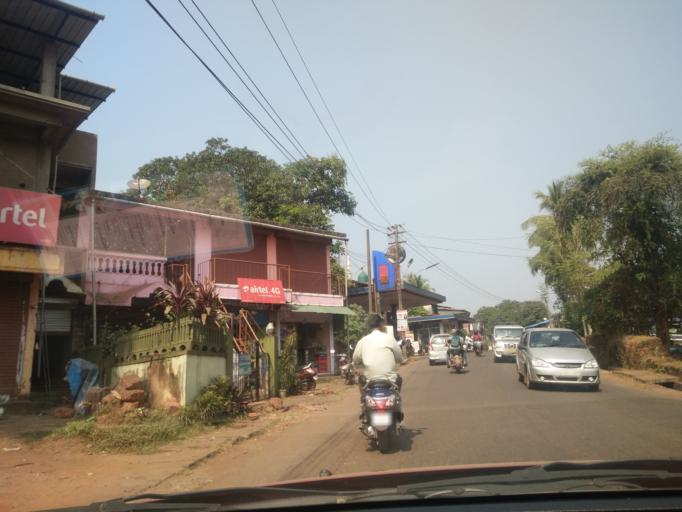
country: IN
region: Goa
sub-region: North Goa
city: Sanquelim
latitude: 15.5629
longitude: 74.0110
